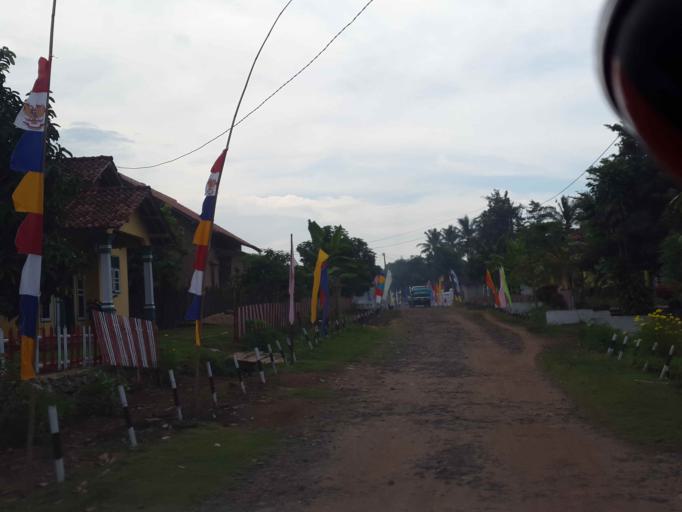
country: ID
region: Lampung
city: Metro
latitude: -5.1963
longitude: 105.2456
